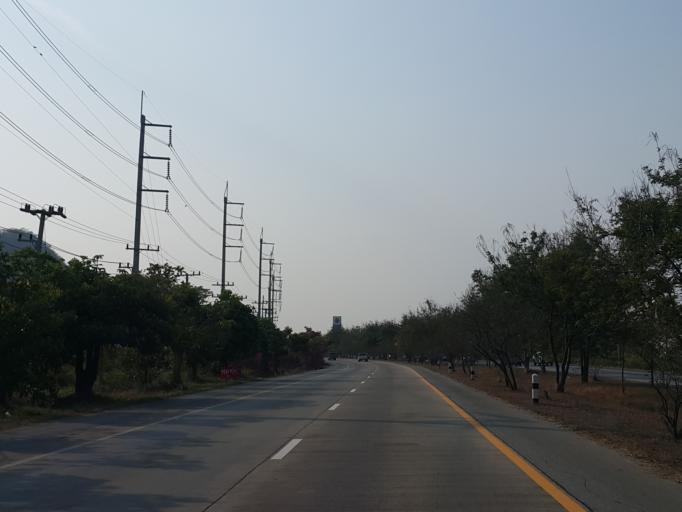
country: TH
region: Suphan Buri
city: Doembang Nangbuat
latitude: 14.8341
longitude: 100.1118
